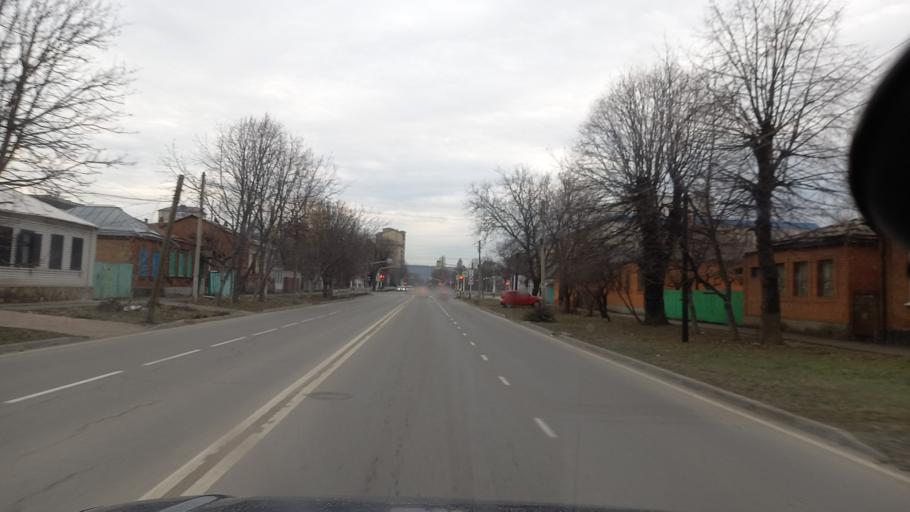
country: RU
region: Adygeya
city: Maykop
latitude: 44.6110
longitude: 40.1008
